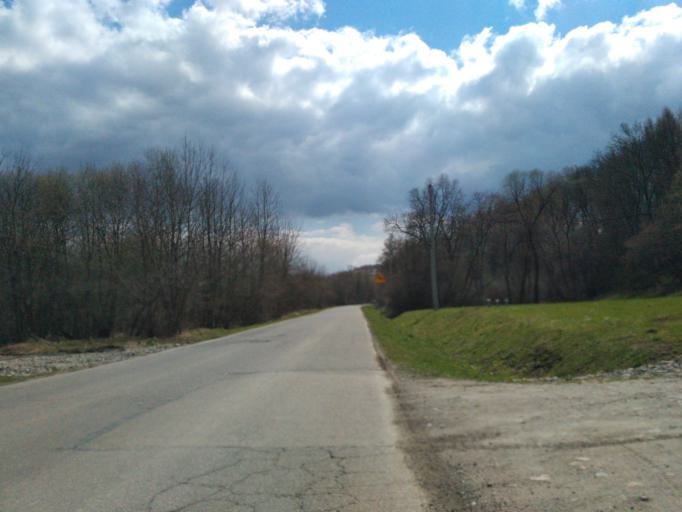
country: PL
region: Subcarpathian Voivodeship
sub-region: Powiat sanocki
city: Tyrawa Woloska
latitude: 49.5862
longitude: 22.3436
